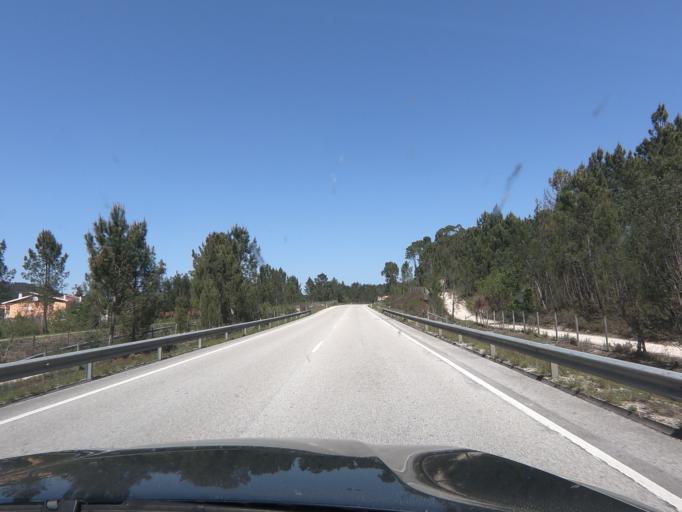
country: PT
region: Coimbra
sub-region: Miranda do Corvo
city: Miranda do Corvo
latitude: 40.1025
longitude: -8.3060
